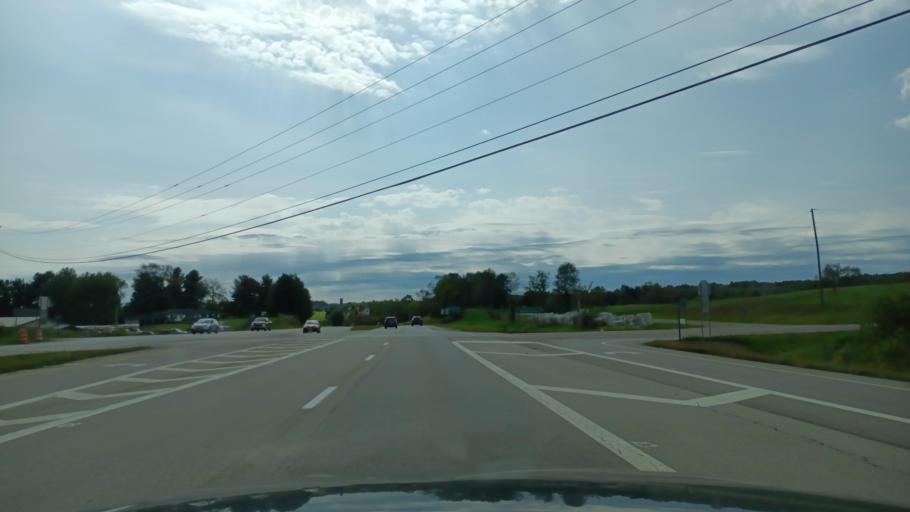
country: US
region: Ohio
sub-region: Athens County
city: Athens
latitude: 39.2824
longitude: -82.1522
